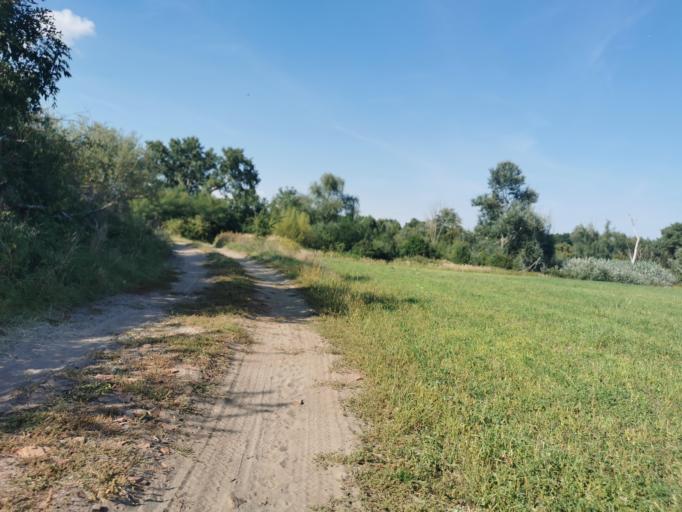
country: SK
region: Trnavsky
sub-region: Okres Senica
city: Senica
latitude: 48.6236
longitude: 17.2318
